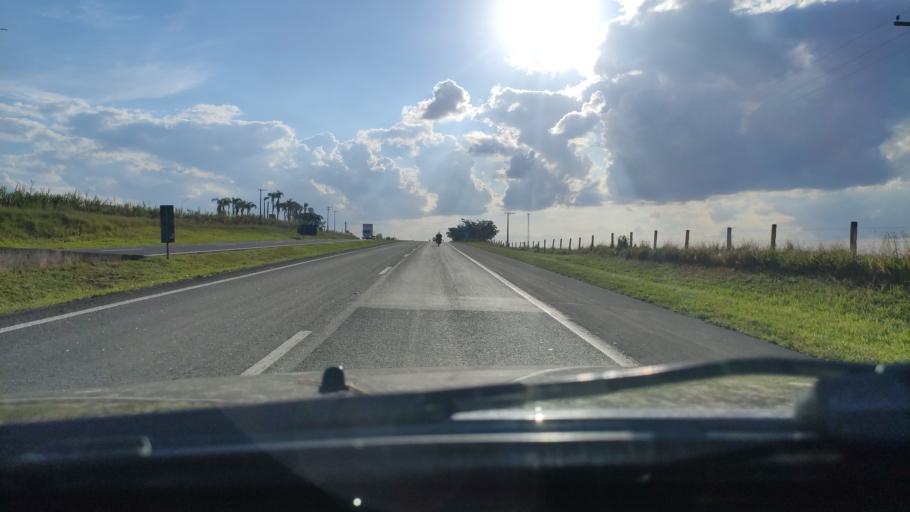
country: BR
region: Sao Paulo
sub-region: Mogi-Mirim
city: Mogi Mirim
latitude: -22.4562
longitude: -46.9117
